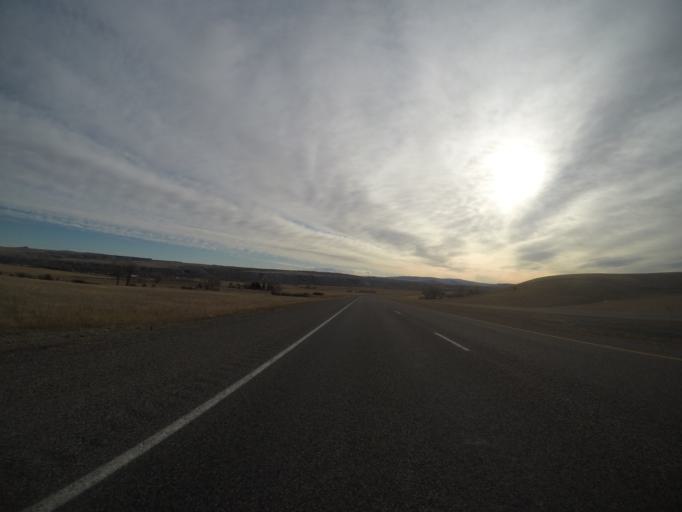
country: US
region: Montana
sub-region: Yellowstone County
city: Laurel
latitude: 45.5438
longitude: -108.8587
